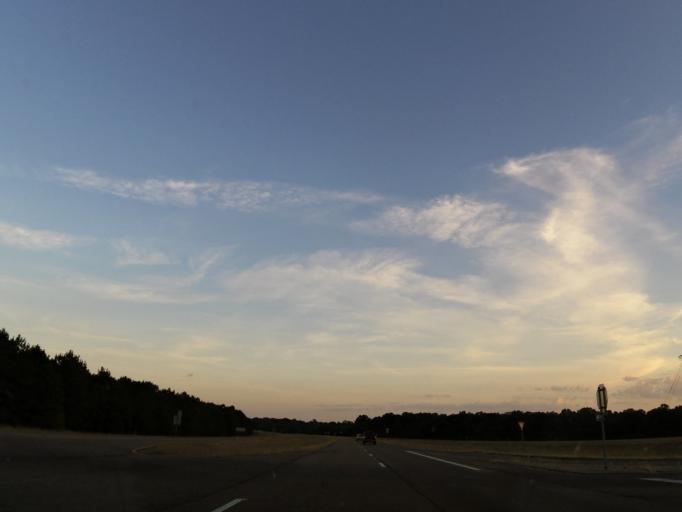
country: US
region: Mississippi
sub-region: Noxubee County
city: Macon
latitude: 32.9773
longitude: -88.5554
